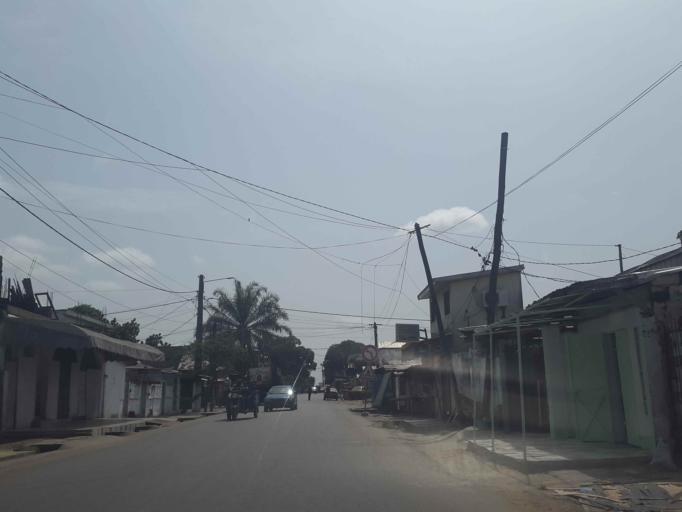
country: CM
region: Littoral
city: Douala
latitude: 4.0691
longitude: 9.7136
